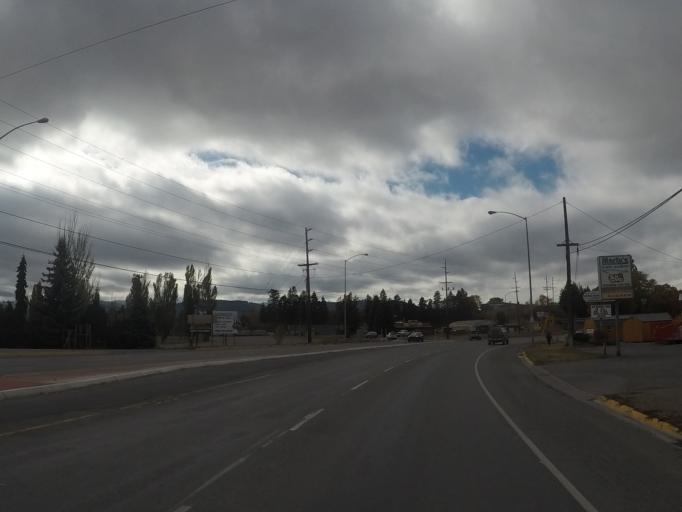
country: US
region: Montana
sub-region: Flathead County
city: Kalispell
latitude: 48.2066
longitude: -114.2951
